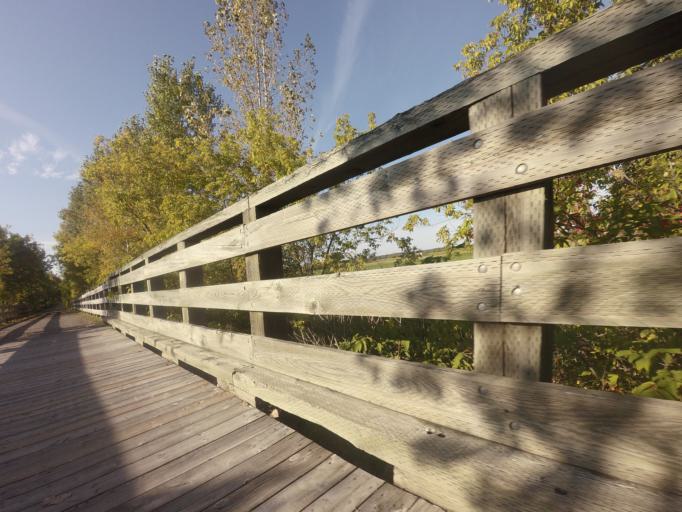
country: CA
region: Quebec
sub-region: Laurentides
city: Saint-Jerome
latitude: 45.7325
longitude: -73.9460
